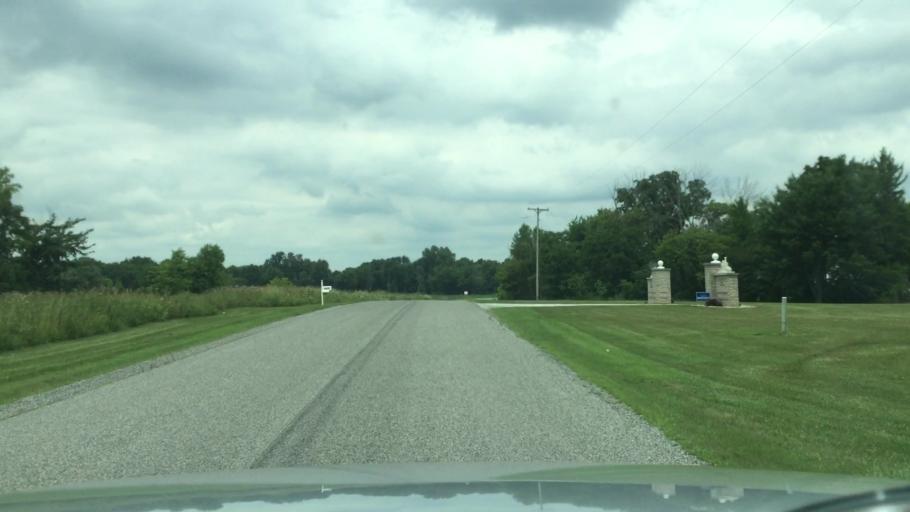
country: US
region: Michigan
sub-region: Saginaw County
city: Burt
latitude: 43.2734
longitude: -83.8856
